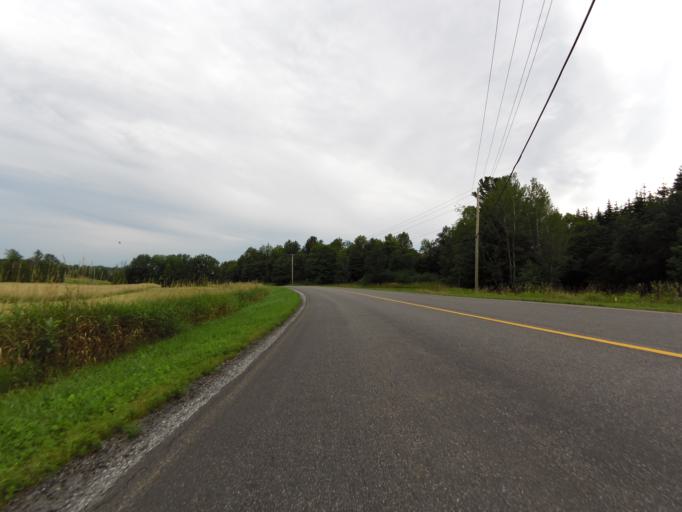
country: CA
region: Ontario
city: Perth
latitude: 45.0611
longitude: -76.3948
